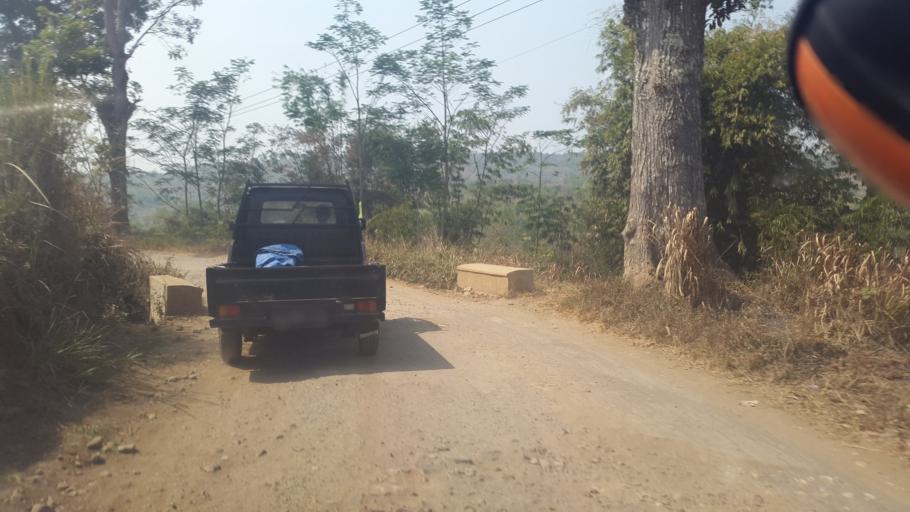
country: ID
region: West Java
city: Pasirlaja
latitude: -7.0536
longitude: 106.8592
